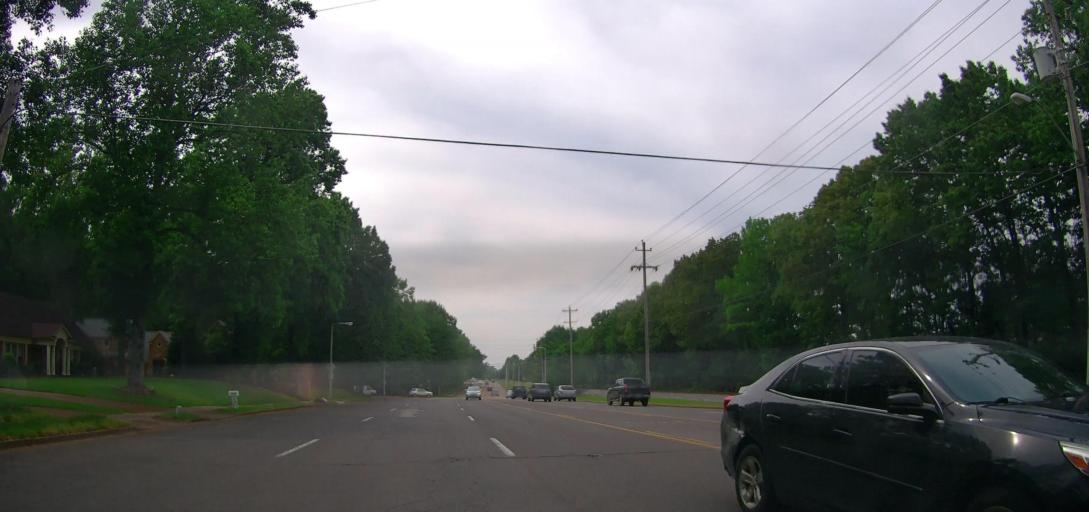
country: US
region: Tennessee
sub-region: Shelby County
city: Germantown
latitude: 35.0965
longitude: -89.8441
